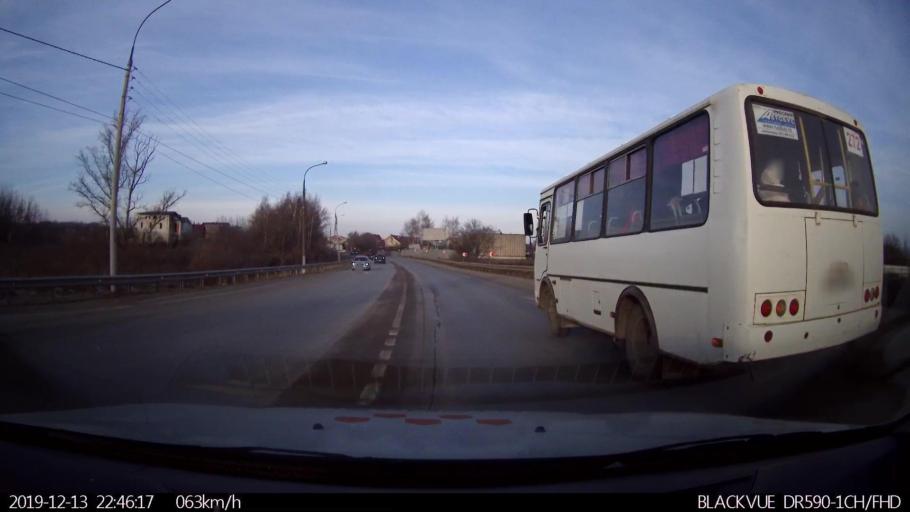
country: RU
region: Nizjnij Novgorod
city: Afonino
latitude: 56.2186
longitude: 44.1056
